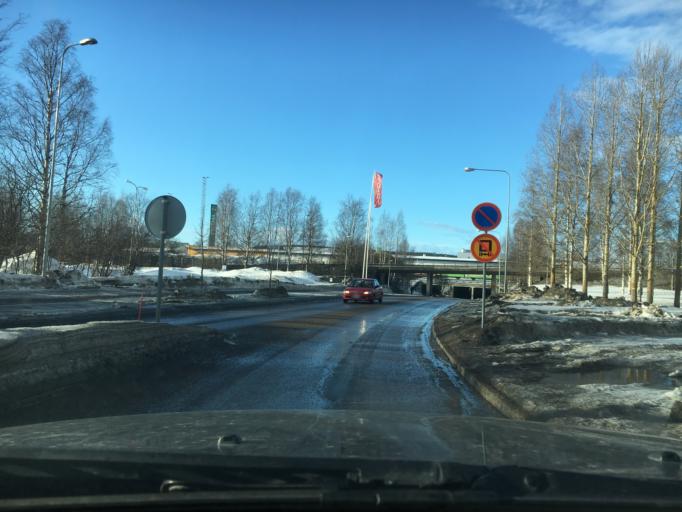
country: FI
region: Kainuu
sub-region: Kajaani
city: Kajaani
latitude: 64.2180
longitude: 27.7458
